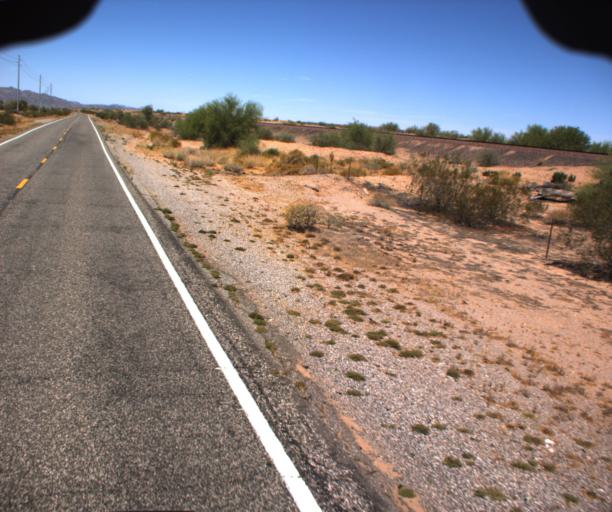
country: US
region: Arizona
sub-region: La Paz County
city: Cienega Springs
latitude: 33.9944
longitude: -114.1389
